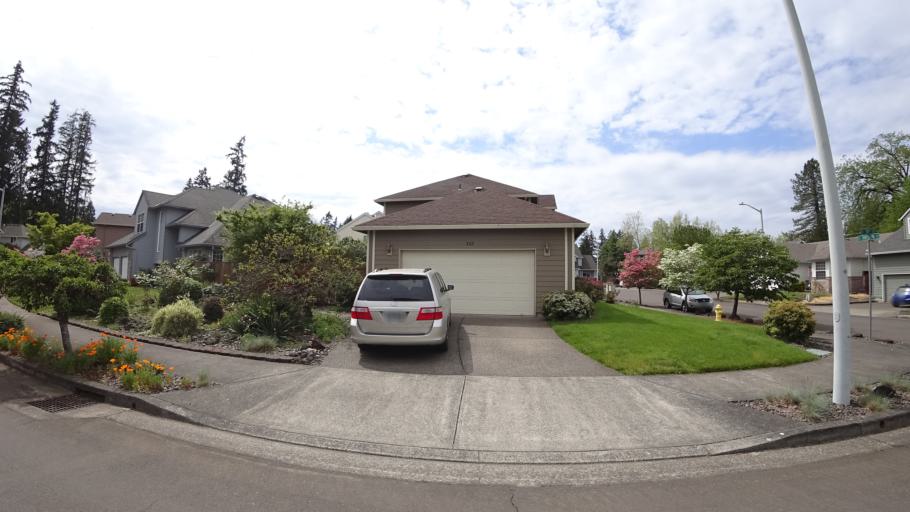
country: US
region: Oregon
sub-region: Washington County
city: Rockcreek
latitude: 45.5186
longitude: -122.9218
